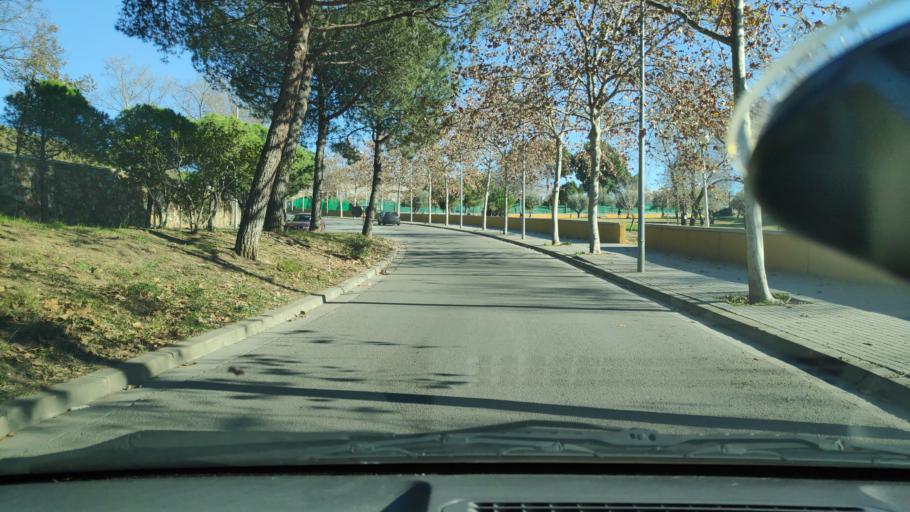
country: ES
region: Catalonia
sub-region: Provincia de Barcelona
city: Sant Quirze del Valles
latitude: 41.5492
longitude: 2.0899
